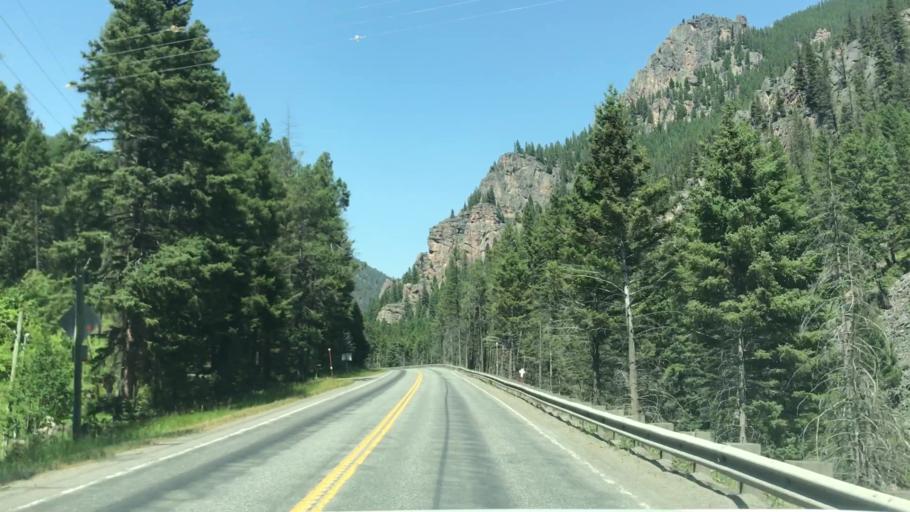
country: US
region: Montana
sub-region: Gallatin County
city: Big Sky
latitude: 45.4104
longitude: -111.2275
